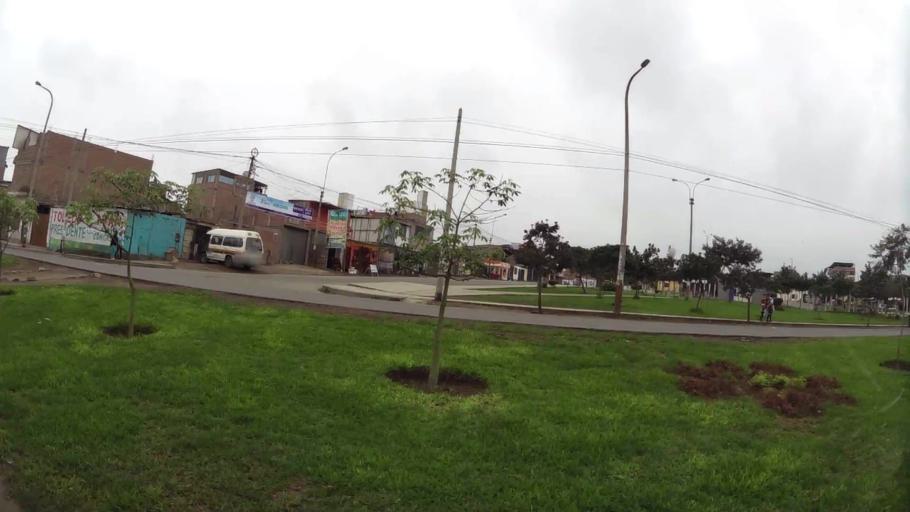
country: PE
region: Lima
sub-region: Lima
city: Punta Hermosa
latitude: -12.2382
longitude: -76.9114
